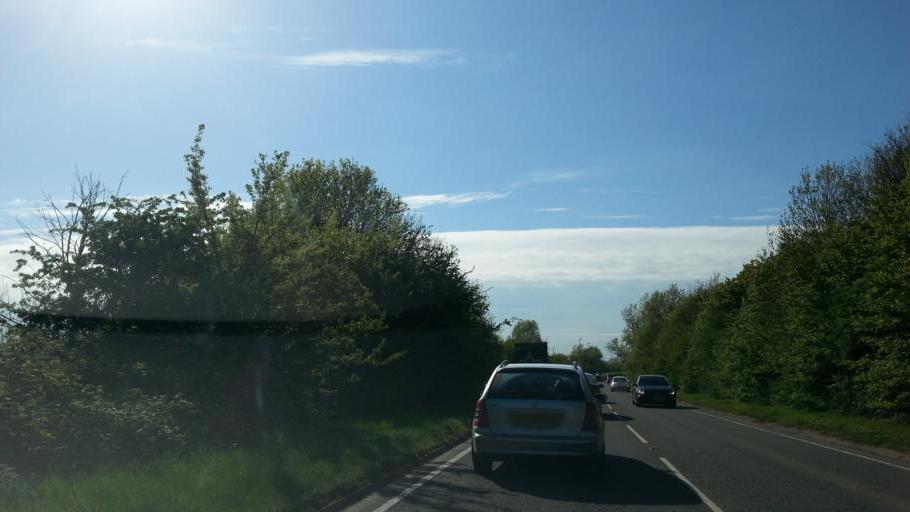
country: GB
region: England
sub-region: Cambridgeshire
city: Witchford
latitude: 52.3917
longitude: 0.1362
